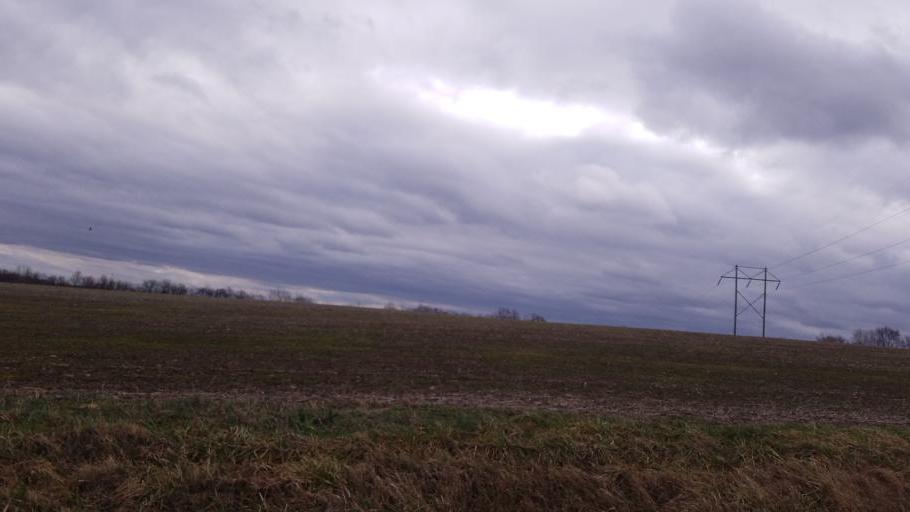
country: US
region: Ohio
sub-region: Knox County
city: Fredericktown
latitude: 40.3955
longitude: -82.6112
